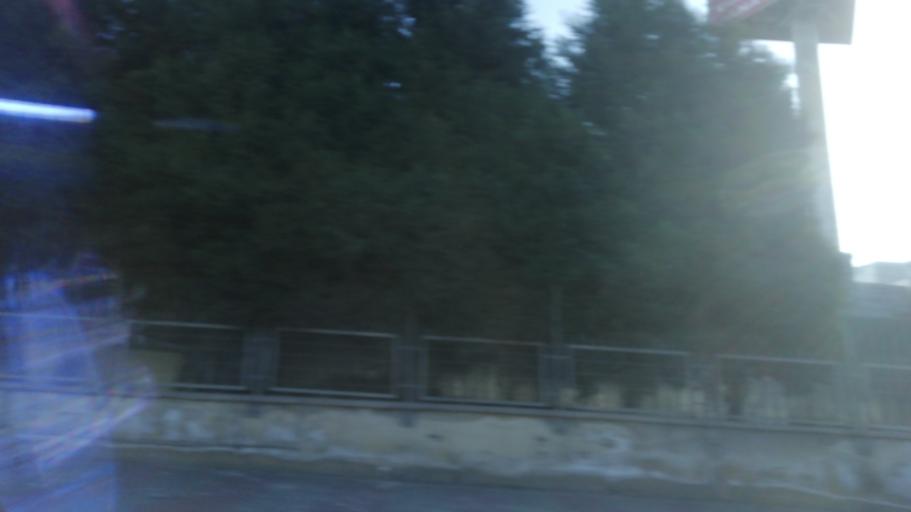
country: TR
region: Istanbul
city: Basaksehir
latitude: 41.0963
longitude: 28.7931
